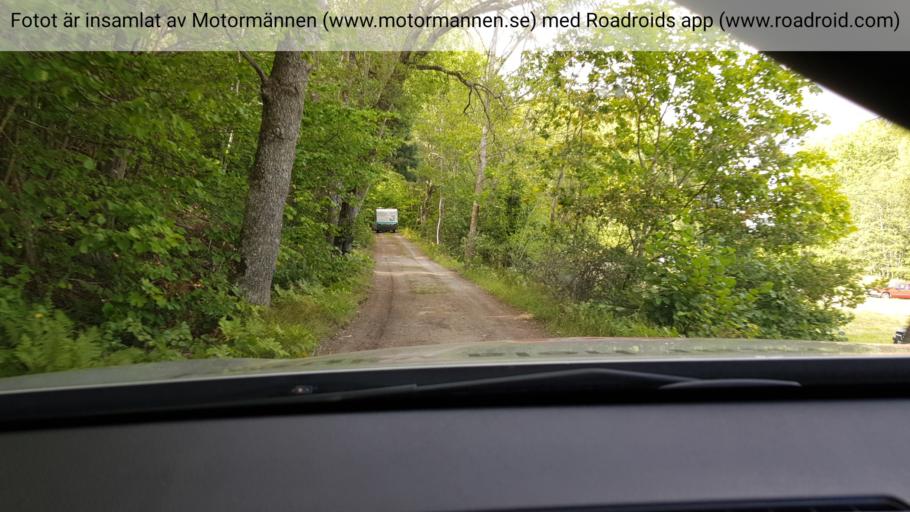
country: SE
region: Stockholm
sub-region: Nynashamns Kommun
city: Osmo
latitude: 58.9384
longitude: 17.9061
